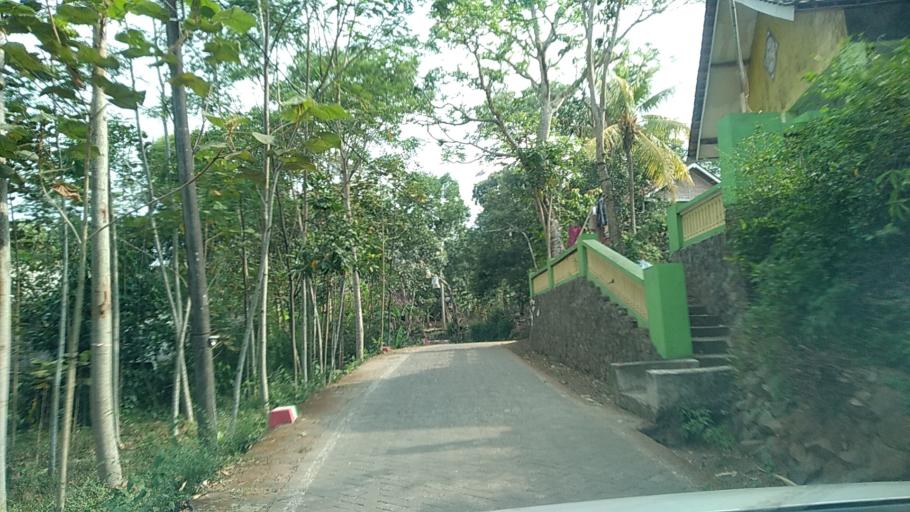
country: ID
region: Central Java
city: Ungaran
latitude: -7.1118
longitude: 110.3871
